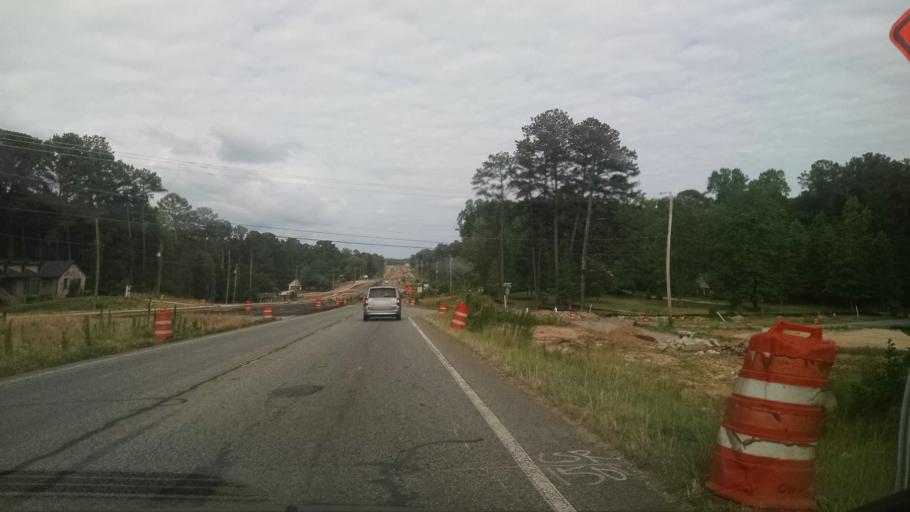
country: US
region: Georgia
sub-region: Gwinnett County
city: Sugar Hill
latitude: 34.1118
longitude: -84.0600
